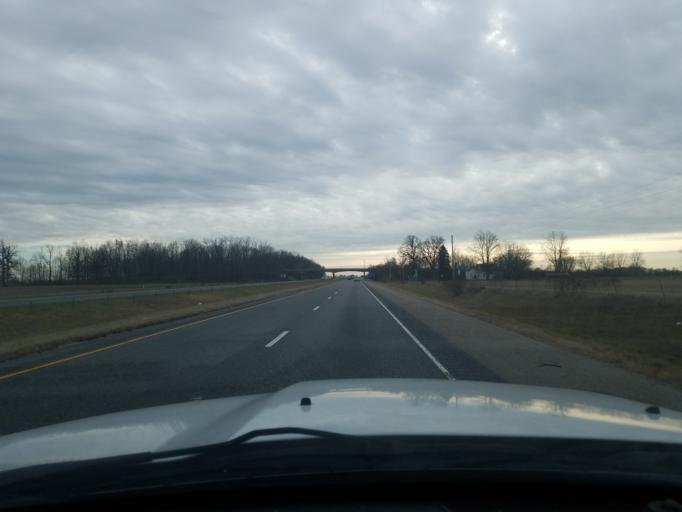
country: US
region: Indiana
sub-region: Grant County
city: Fairmount
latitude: 40.3675
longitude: -85.5591
